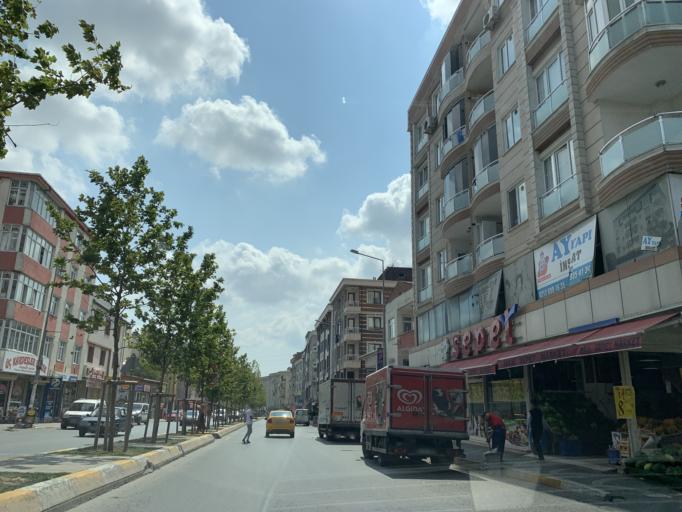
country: TR
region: Istanbul
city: Esenyurt
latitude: 41.0450
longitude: 28.6658
